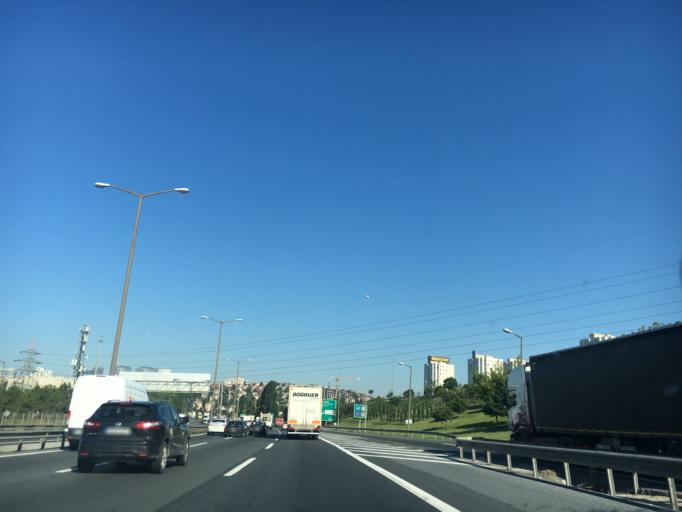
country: TR
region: Istanbul
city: Esenyurt
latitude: 41.0581
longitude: 28.7076
